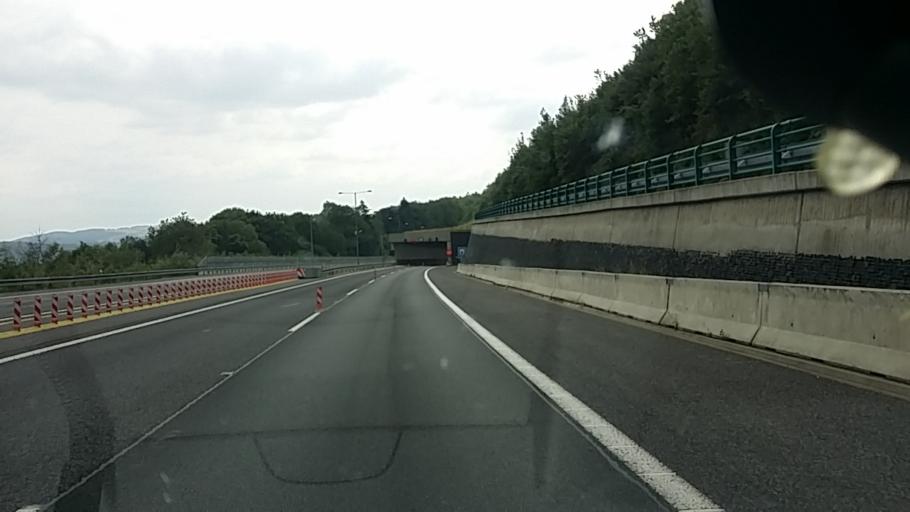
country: CZ
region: Ustecky
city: Libouchec
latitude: 50.7492
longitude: 14.0005
